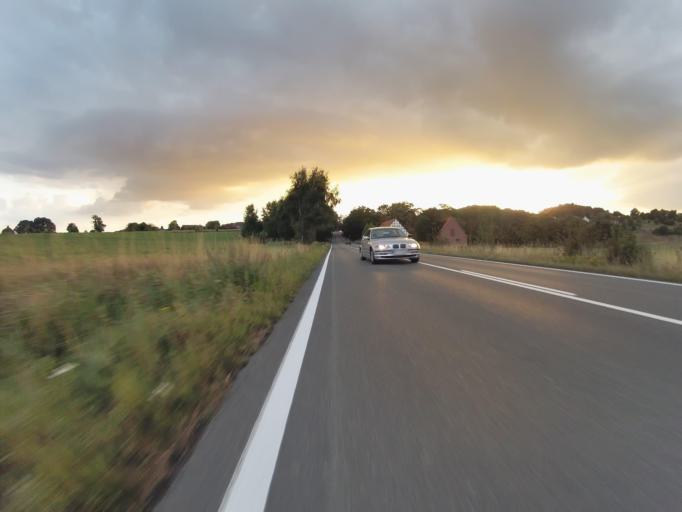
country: DE
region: North Rhine-Westphalia
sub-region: Regierungsbezirk Munster
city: Tecklenburg
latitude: 52.2757
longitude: 7.8353
